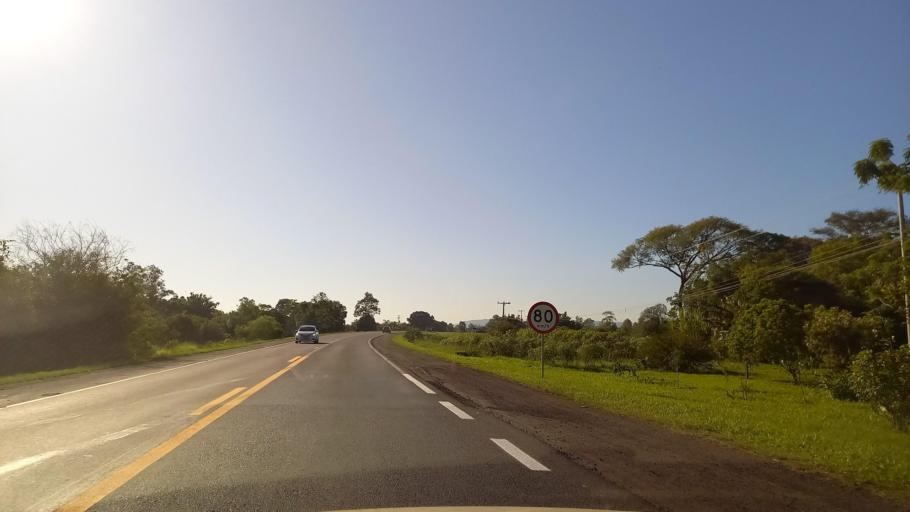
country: BR
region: Rio Grande do Sul
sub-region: Venancio Aires
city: Venancio Aires
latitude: -29.6684
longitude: -52.0323
